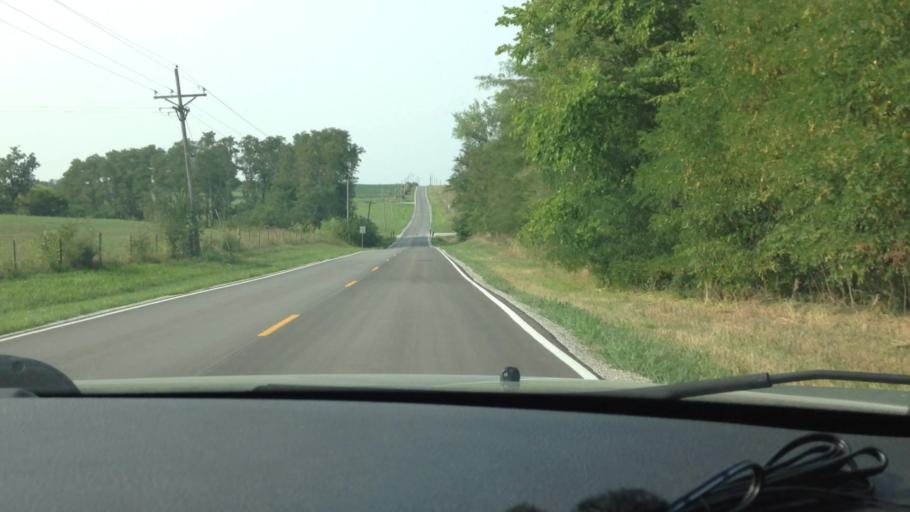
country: US
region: Missouri
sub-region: Platte County
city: Platte City
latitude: 39.4314
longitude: -94.7798
